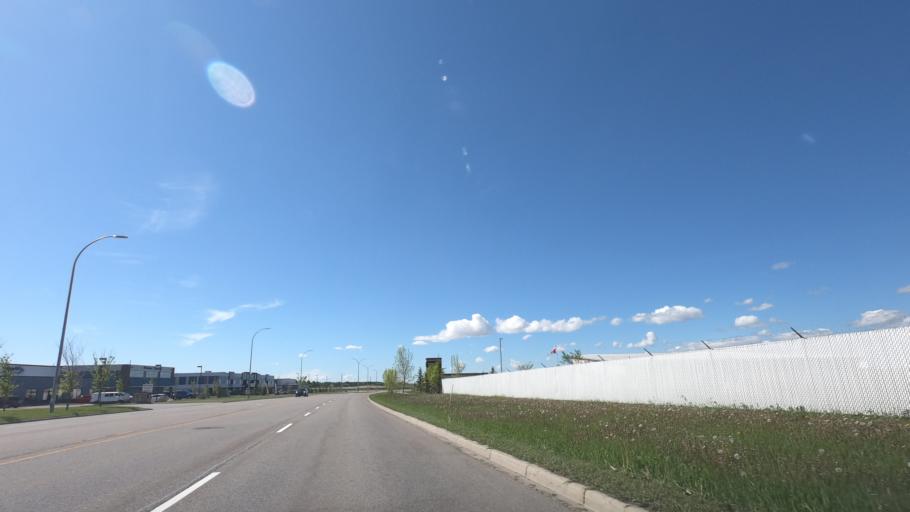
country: CA
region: Alberta
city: Airdrie
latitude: 51.2594
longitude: -113.9953
